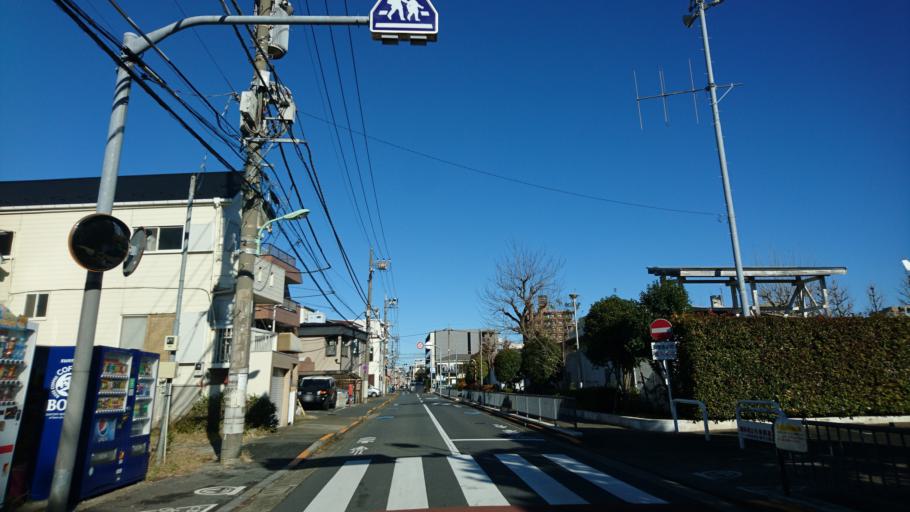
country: JP
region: Kanagawa
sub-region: Kawasaki-shi
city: Kawasaki
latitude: 35.5502
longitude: 139.7360
